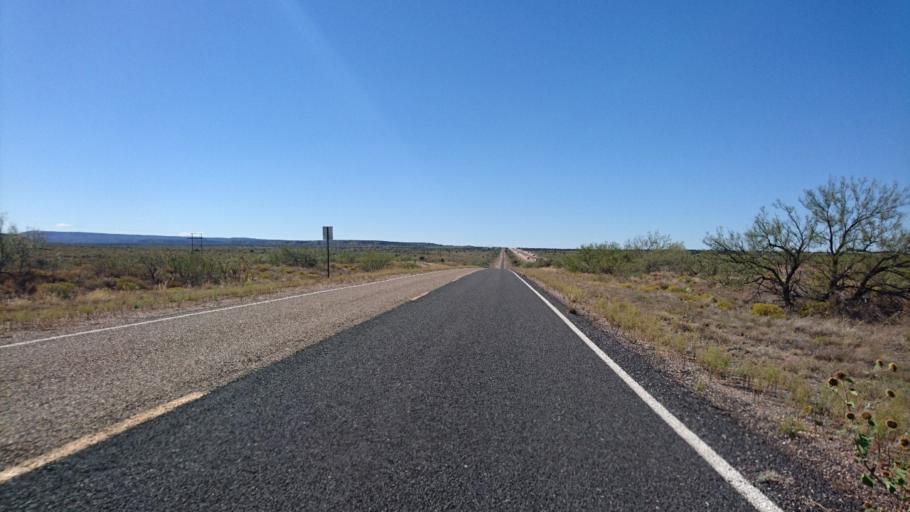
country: US
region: New Mexico
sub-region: Quay County
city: Tucumcari
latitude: 35.0771
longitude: -104.1342
